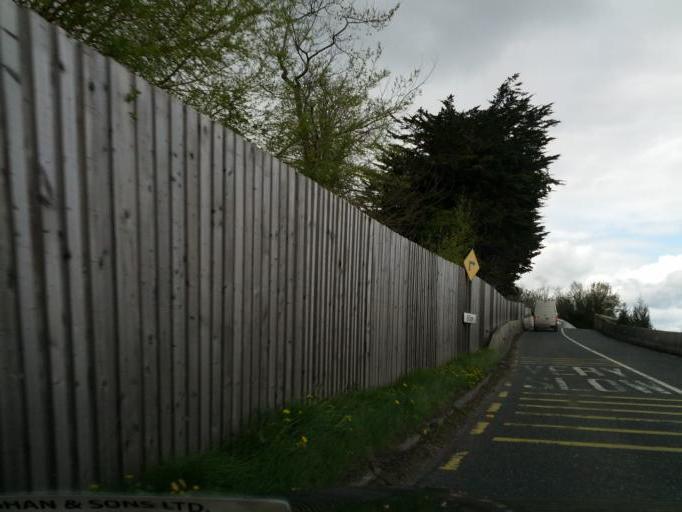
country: IE
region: Leinster
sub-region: An Mhi
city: Dunboyne
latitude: 53.3890
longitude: -6.4494
